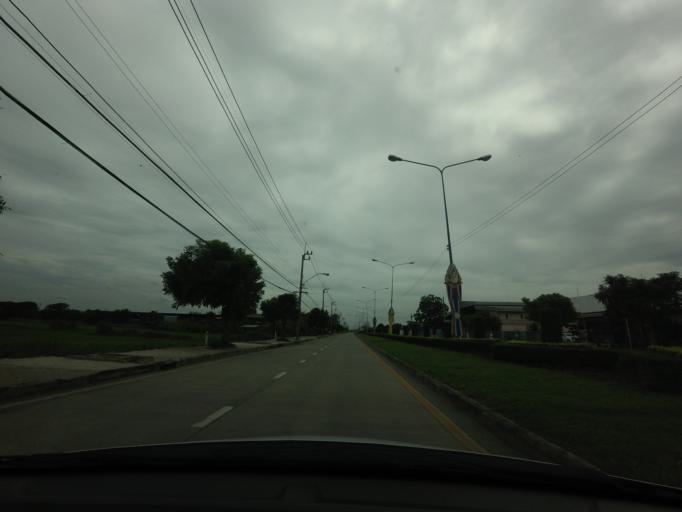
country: TH
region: Pathum Thani
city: Lam Luk Ka
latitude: 13.9111
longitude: 100.7607
